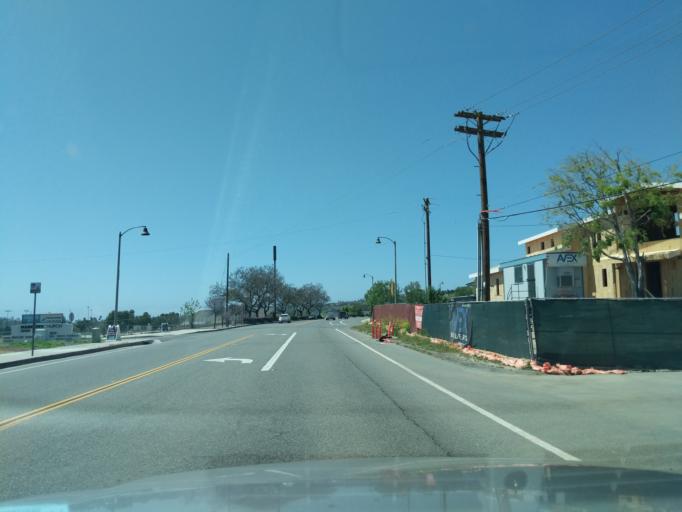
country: US
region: California
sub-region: Orange County
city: San Juan Capistrano
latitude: 33.4951
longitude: -117.6760
